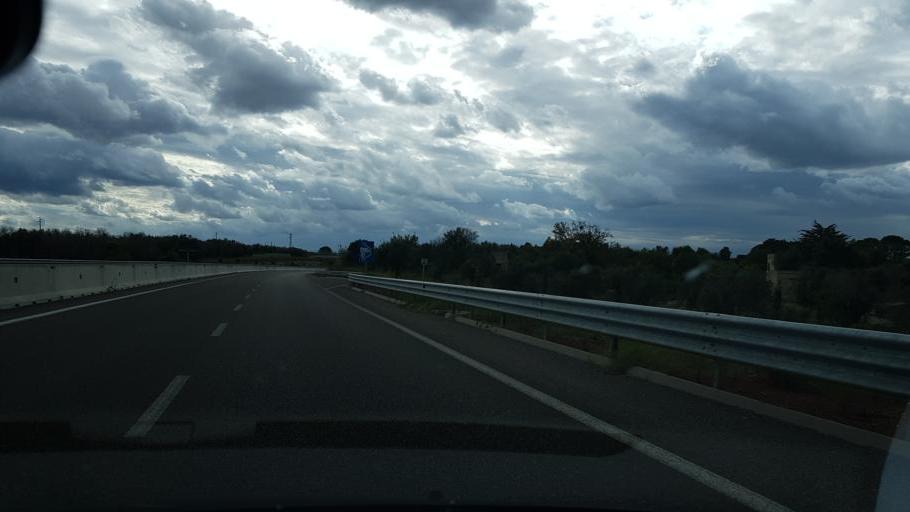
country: IT
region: Apulia
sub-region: Provincia di Lecce
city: Palmariggi
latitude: 40.1289
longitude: 18.3865
